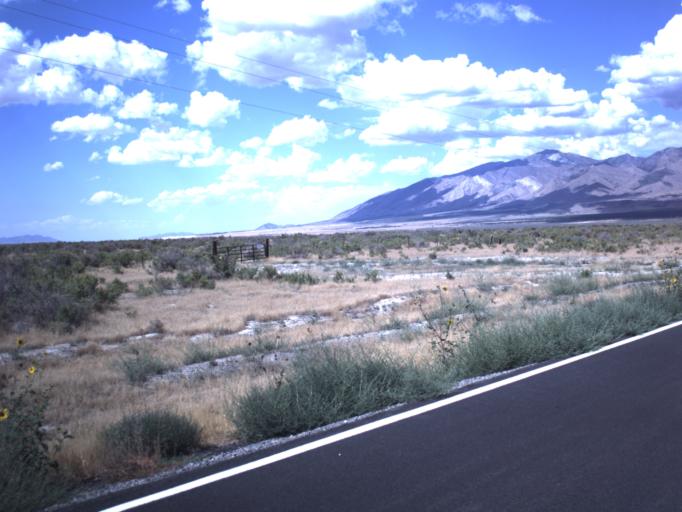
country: US
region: Utah
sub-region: Tooele County
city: Grantsville
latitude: 40.2527
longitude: -112.7009
